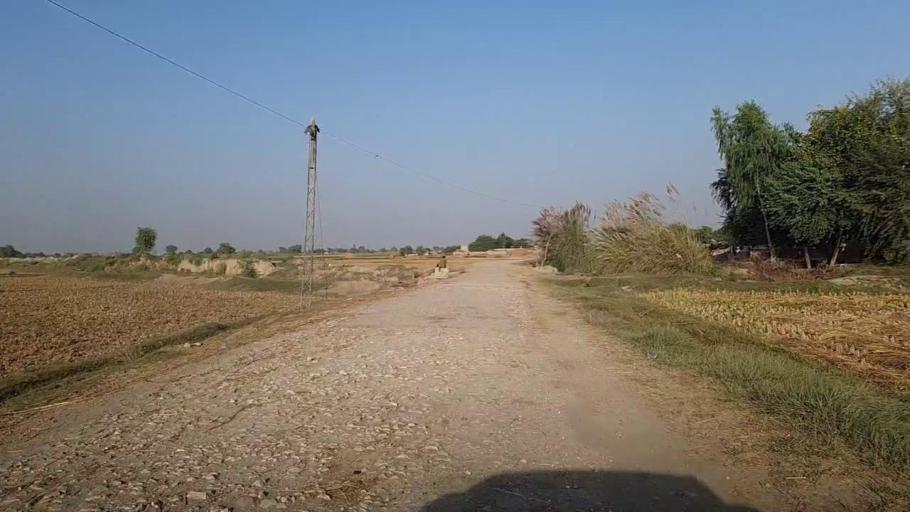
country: PK
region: Sindh
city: Kashmor
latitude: 28.4221
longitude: 69.4215
